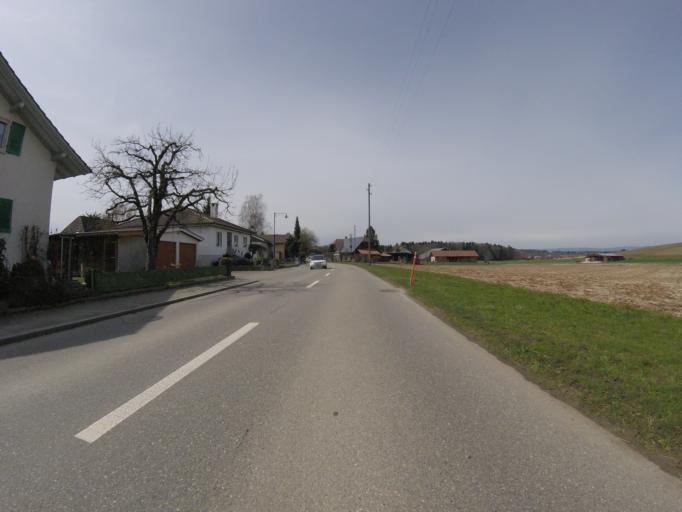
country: CH
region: Fribourg
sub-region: Sense District
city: Bosingen
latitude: 46.9104
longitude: 7.2213
